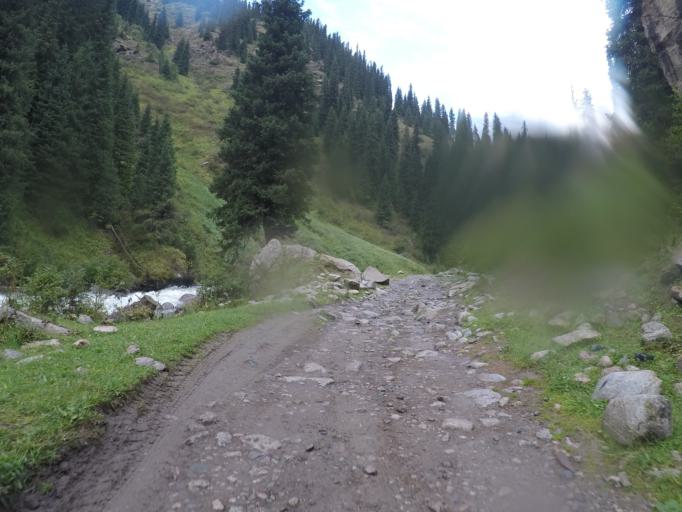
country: KG
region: Ysyk-Koel
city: Teploklyuchenka
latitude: 42.4147
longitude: 78.5715
